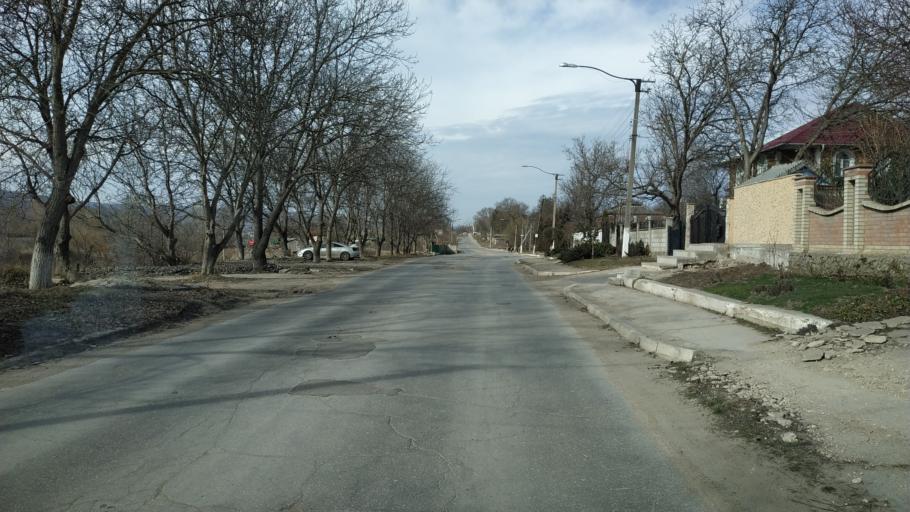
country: MD
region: Chisinau
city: Vatra
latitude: 47.0905
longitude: 28.6865
